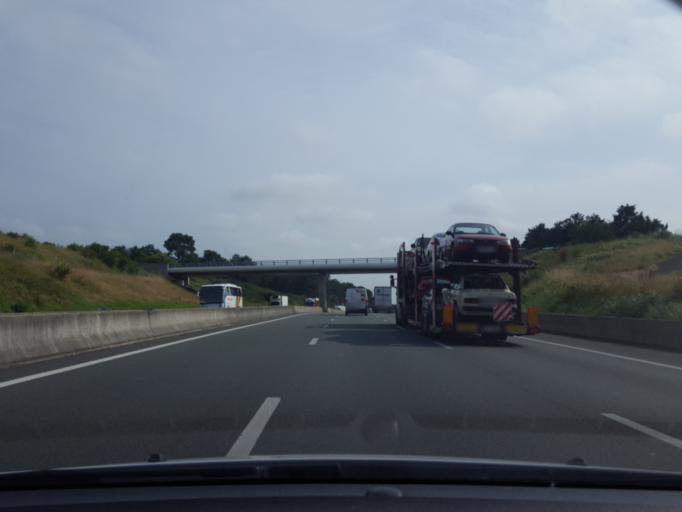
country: FR
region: Aquitaine
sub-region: Departement des Pyrenees-Atlantiques
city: Boucau
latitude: 43.5238
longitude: -1.4404
